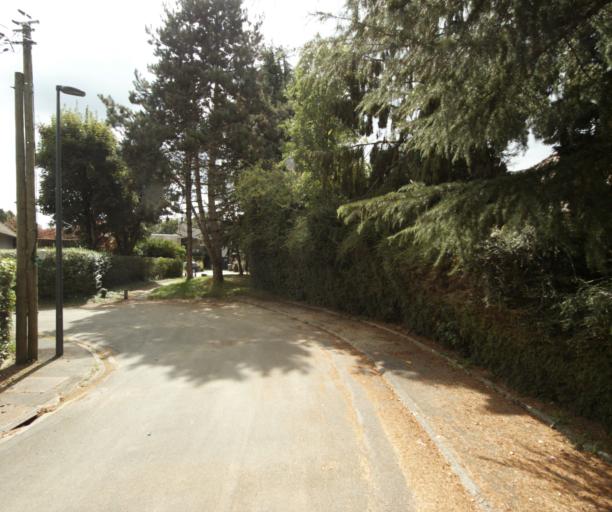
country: FR
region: Nord-Pas-de-Calais
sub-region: Departement du Nord
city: Villeneuve-d'Ascq
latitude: 50.6165
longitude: 3.1517
